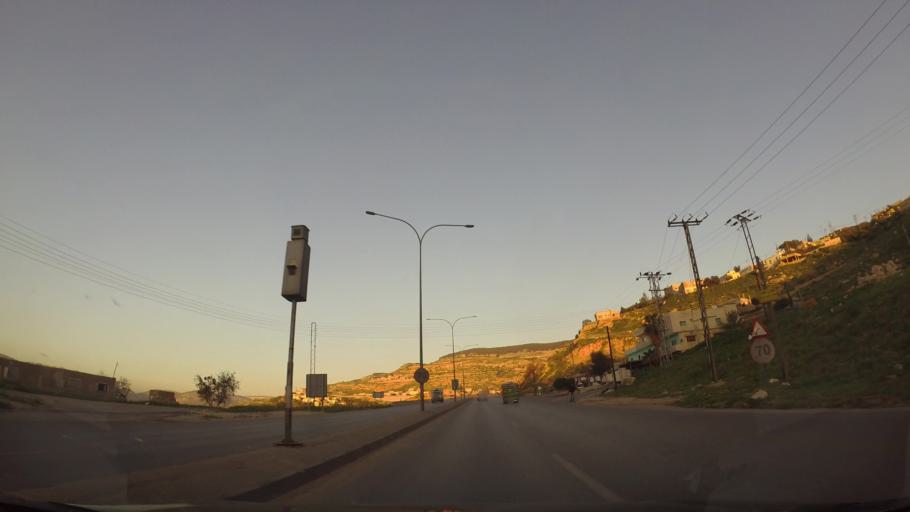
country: JO
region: Amman
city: Umm as Summaq
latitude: 31.8633
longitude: 35.7541
